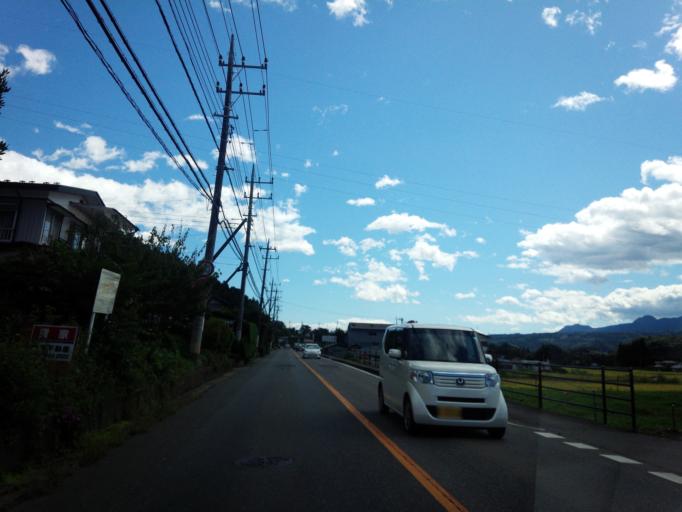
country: JP
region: Gunma
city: Nakanojomachi
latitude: 36.5966
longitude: 138.8093
